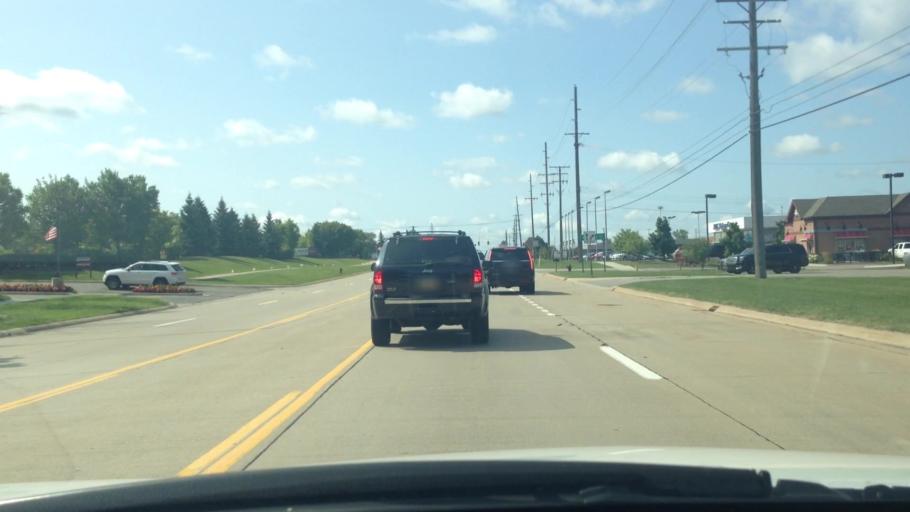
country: US
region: Michigan
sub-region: Oakland County
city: Wolverine Lake
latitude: 42.5582
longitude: -83.4393
